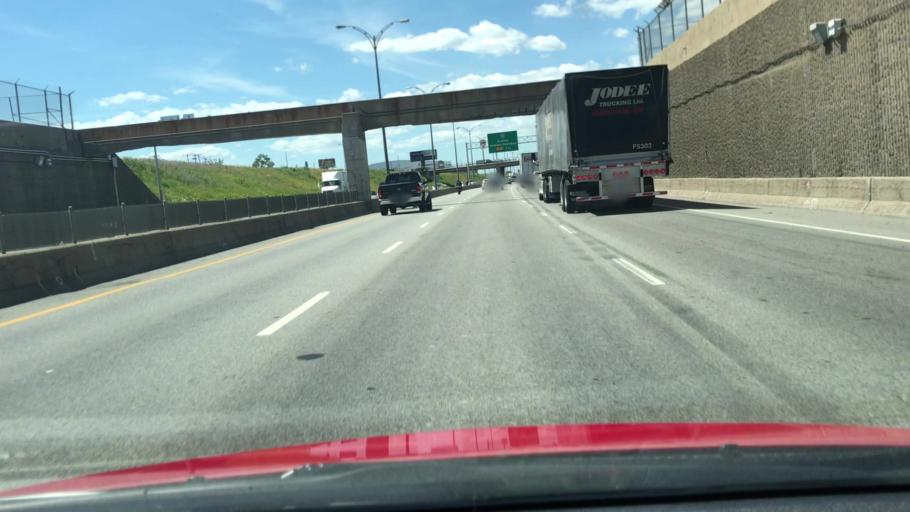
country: CA
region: Quebec
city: Dorval
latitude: 45.4807
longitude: -73.7200
